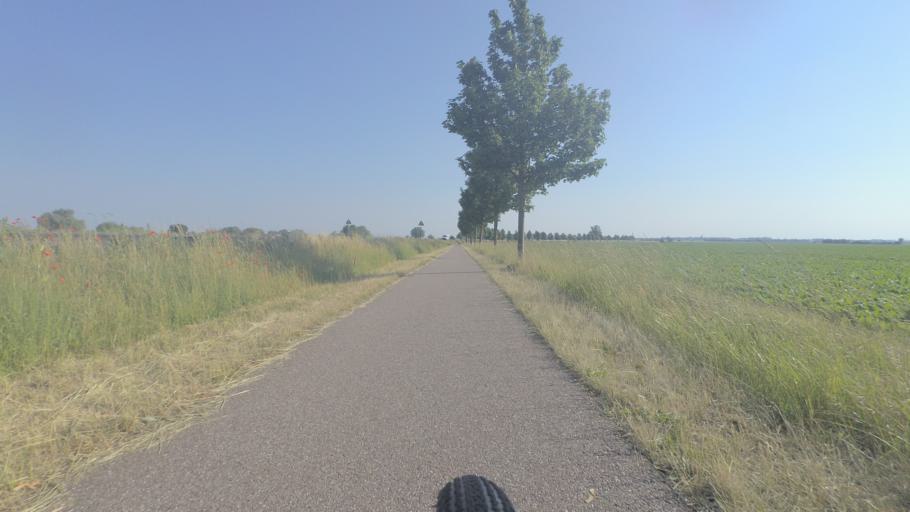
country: DE
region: Saxony-Anhalt
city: Osternienburger Land
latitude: 51.7771
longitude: 12.0002
